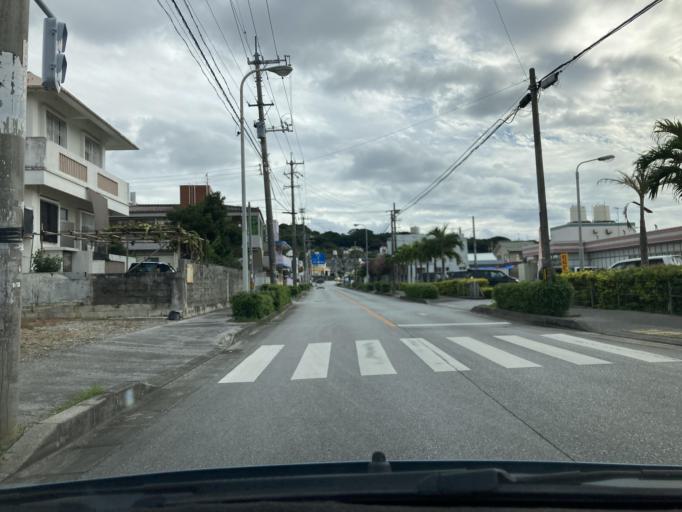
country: JP
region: Okinawa
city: Itoman
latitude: 26.1264
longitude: 127.6773
